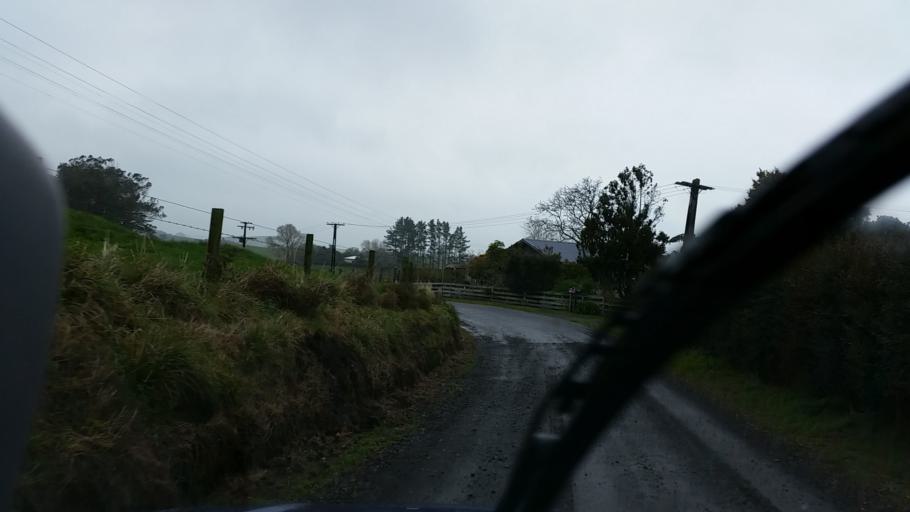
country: NZ
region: Taranaki
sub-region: South Taranaki District
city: Eltham
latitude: -39.2832
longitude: 174.3379
